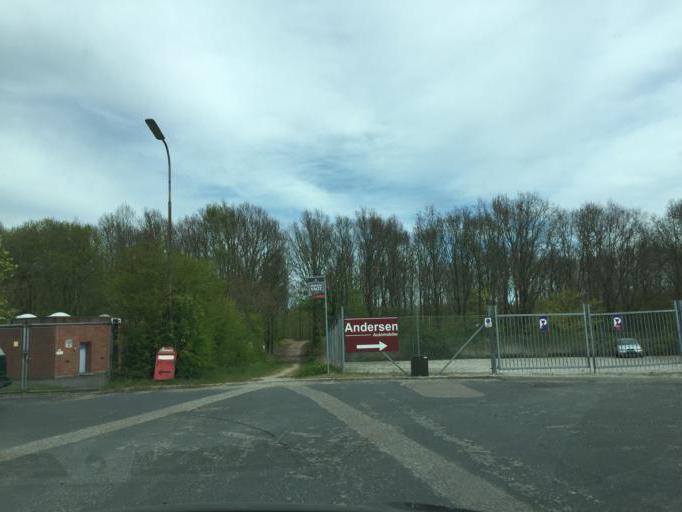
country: DK
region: South Denmark
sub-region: Odense Kommune
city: Odense
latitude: 55.4177
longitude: 10.3431
